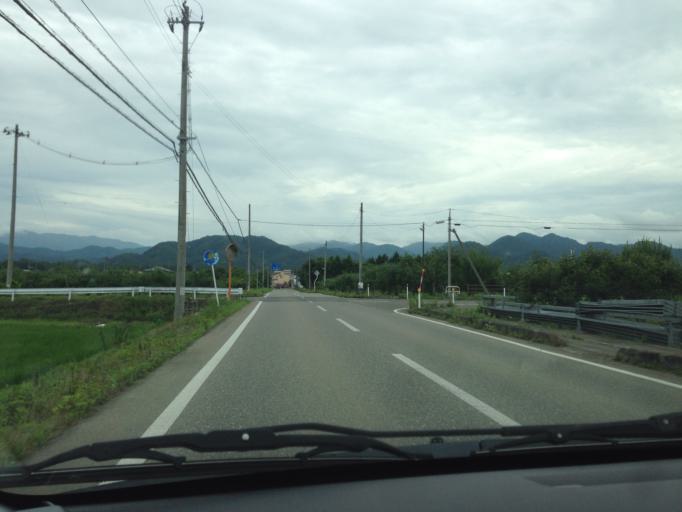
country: JP
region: Fukushima
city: Kitakata
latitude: 37.4466
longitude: 139.8468
